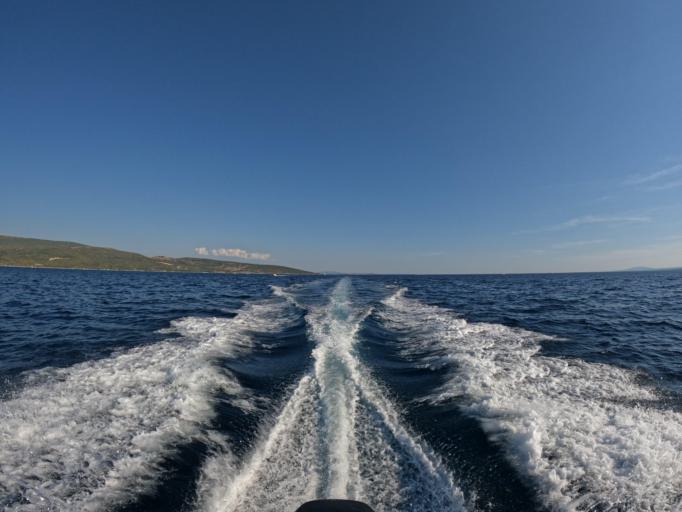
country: HR
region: Primorsko-Goranska
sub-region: Grad Krk
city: Krk
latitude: 45.0079
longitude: 14.5922
